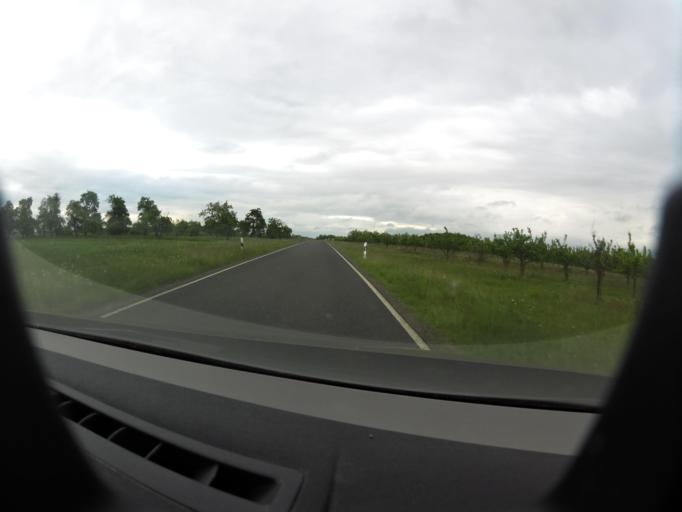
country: DE
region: Bavaria
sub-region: Regierungsbezirk Unterfranken
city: Nordheim
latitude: 49.8814
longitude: 10.1903
